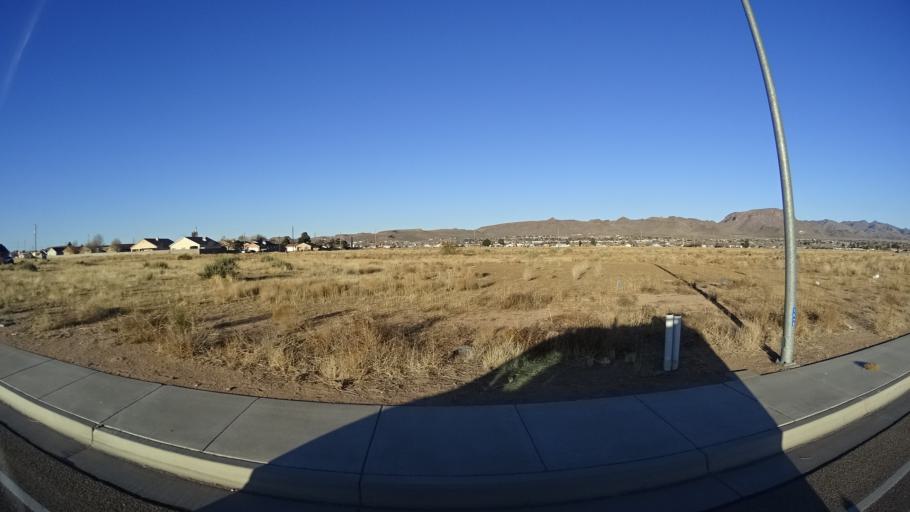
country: US
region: Arizona
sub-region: Mohave County
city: New Kingman-Butler
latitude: 35.2291
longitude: -114.0114
